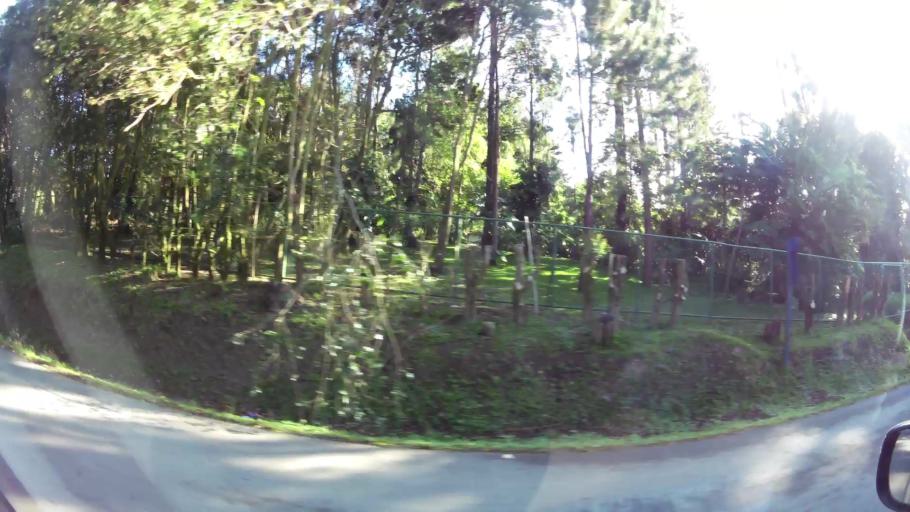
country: CR
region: Guanacaste
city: Juntas
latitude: 10.3118
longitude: -84.8155
